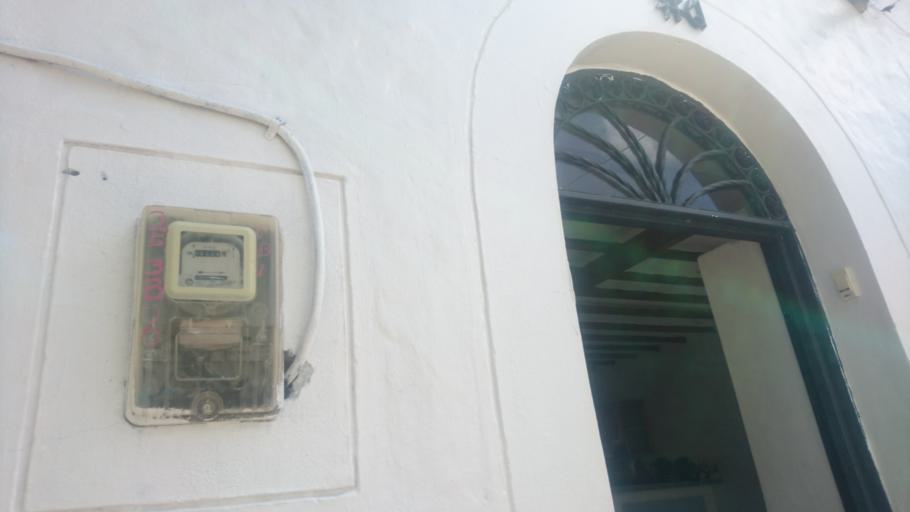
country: CO
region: Antioquia
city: Puerto Triunfo
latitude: 5.9000
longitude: -74.7394
